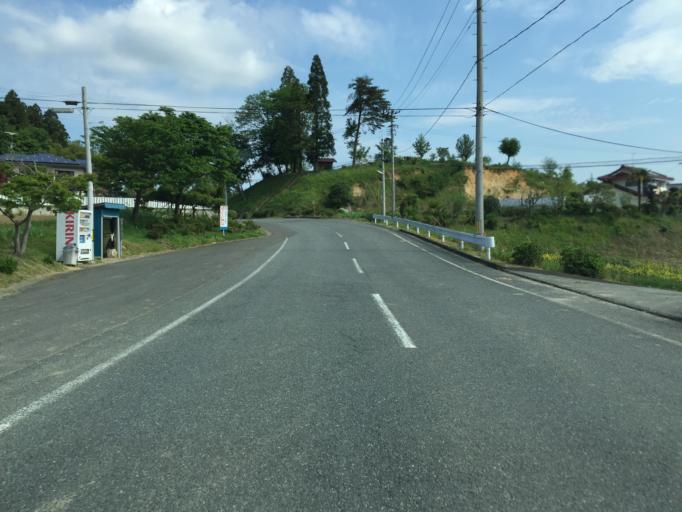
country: JP
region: Fukushima
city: Fukushima-shi
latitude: 37.6626
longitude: 140.4960
